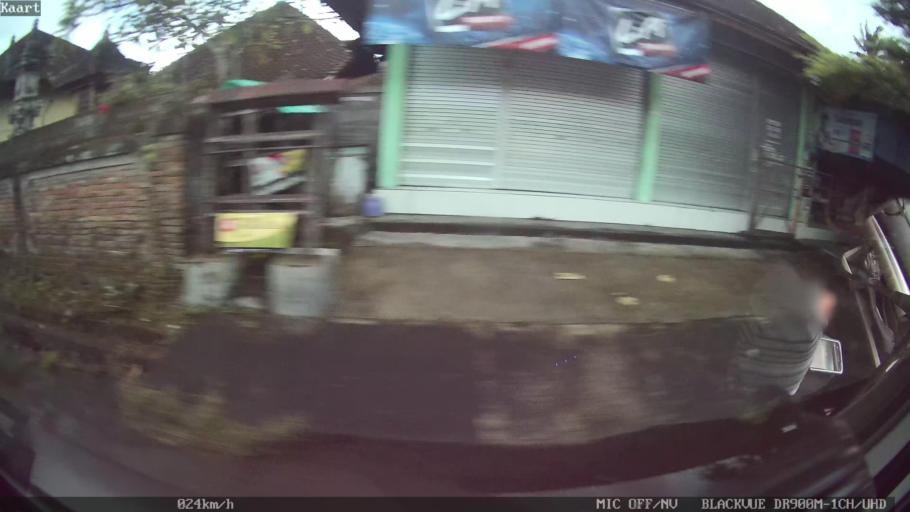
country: ID
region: Bali
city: Banjar Pande
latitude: -8.5220
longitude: 115.2289
